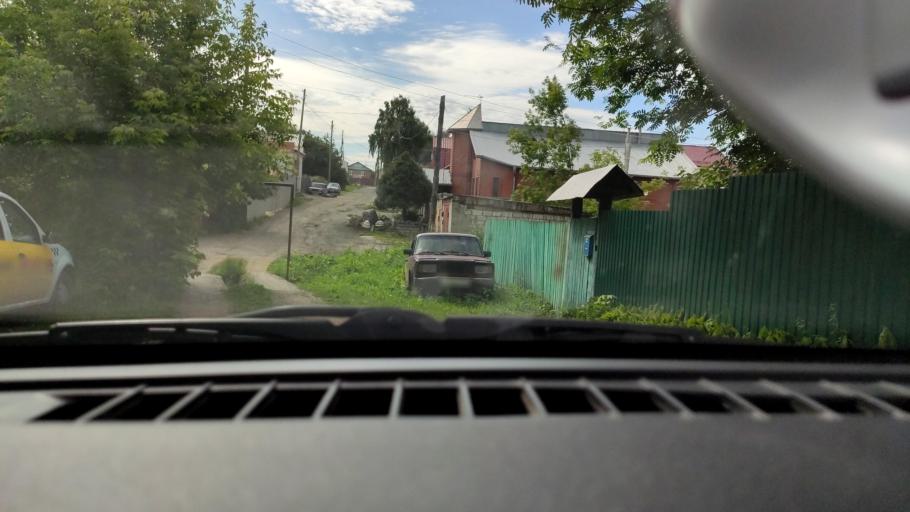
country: RU
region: Perm
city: Kondratovo
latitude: 57.9670
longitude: 56.1405
